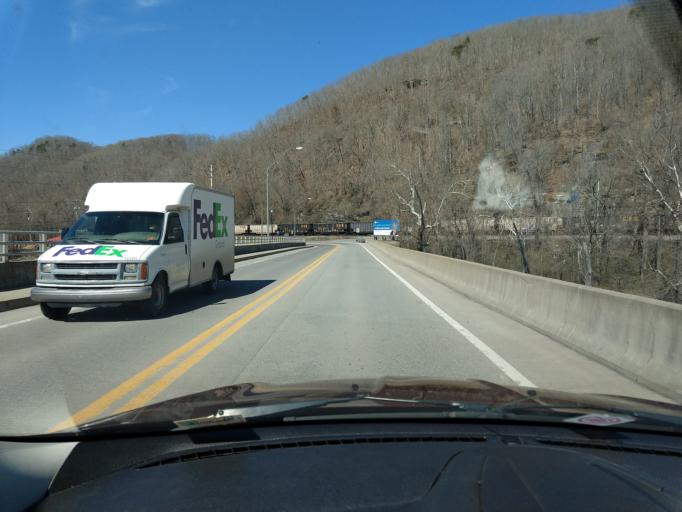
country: US
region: West Virginia
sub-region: Summers County
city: Hinton
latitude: 37.6532
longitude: -80.8844
